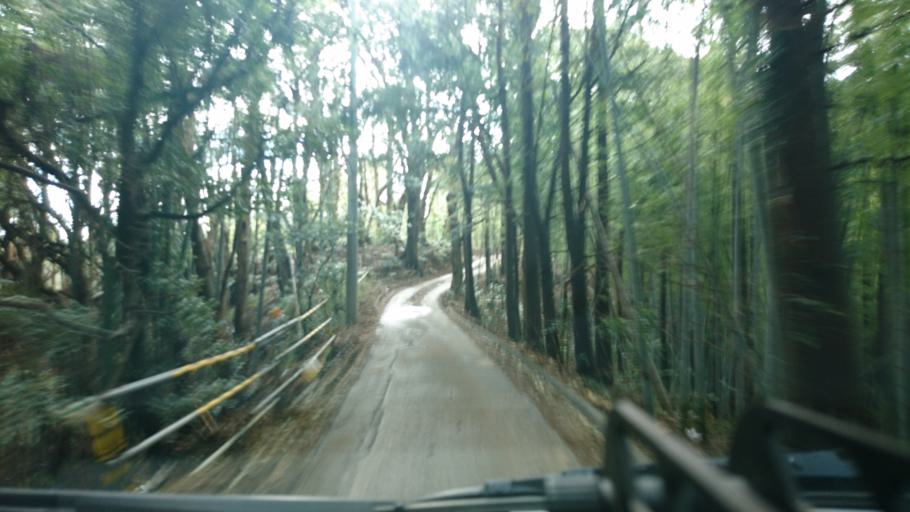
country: JP
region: Chiba
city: Kisarazu
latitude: 35.3328
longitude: 139.9606
